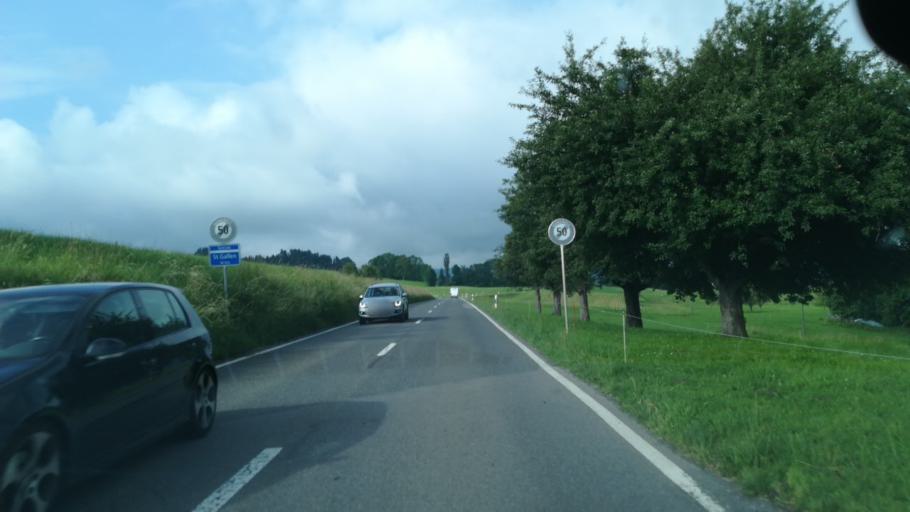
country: CH
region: Saint Gallen
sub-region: Wahlkreis St. Gallen
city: Gossau
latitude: 47.4366
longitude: 9.2516
